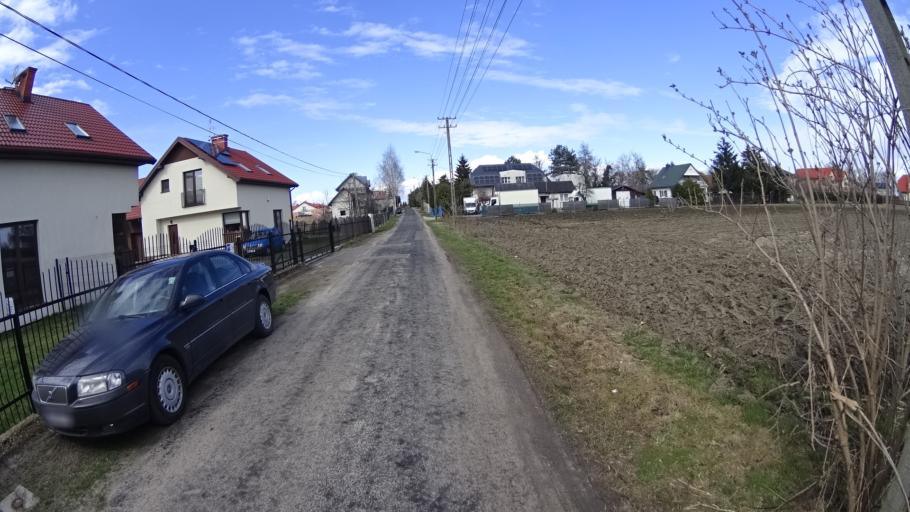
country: PL
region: Masovian Voivodeship
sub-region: Powiat warszawski zachodni
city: Jozefow
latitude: 52.2042
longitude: 20.6841
